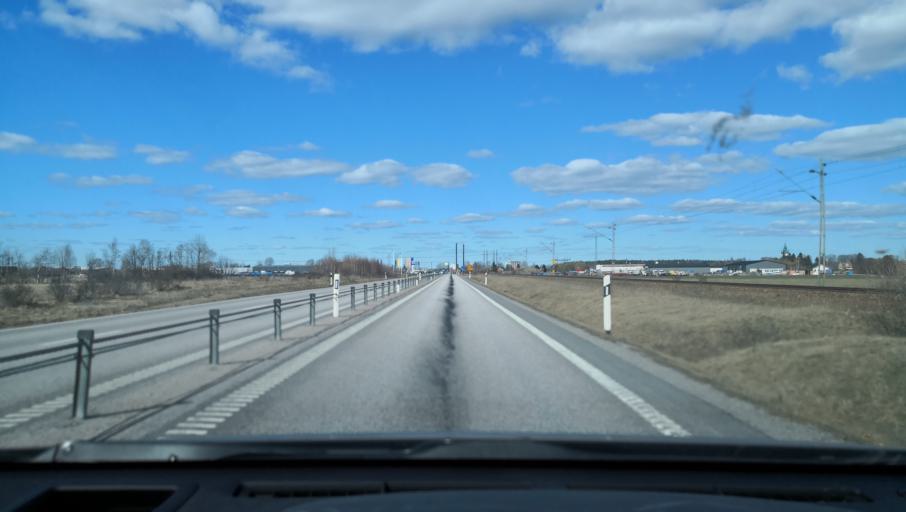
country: SE
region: Vaestmanland
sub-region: Sala Kommun
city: Sala
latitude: 59.9050
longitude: 16.6206
